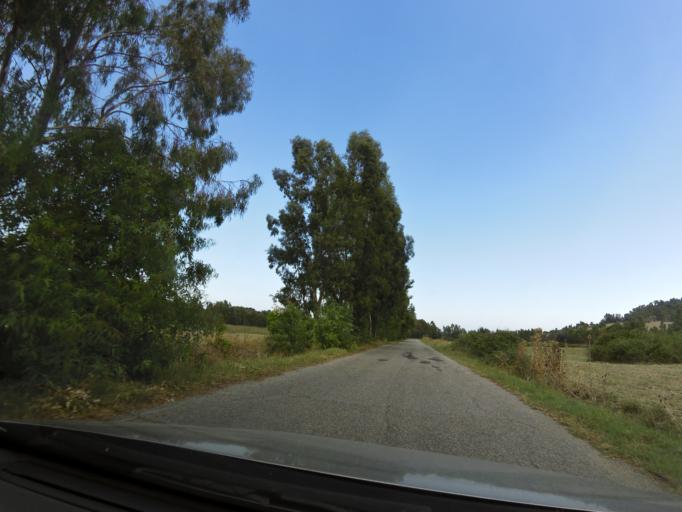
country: IT
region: Calabria
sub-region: Provincia di Reggio Calabria
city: Monasterace
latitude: 38.4278
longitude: 16.5265
